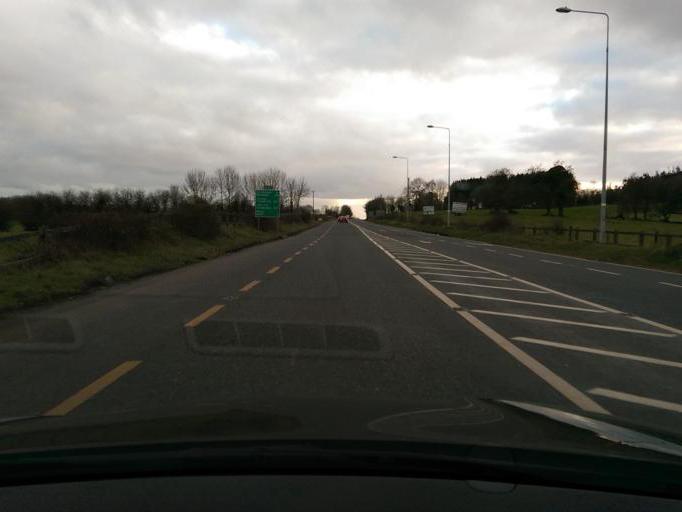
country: IE
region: Leinster
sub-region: Uibh Fhaili
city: Birr
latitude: 53.1173
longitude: -7.8903
